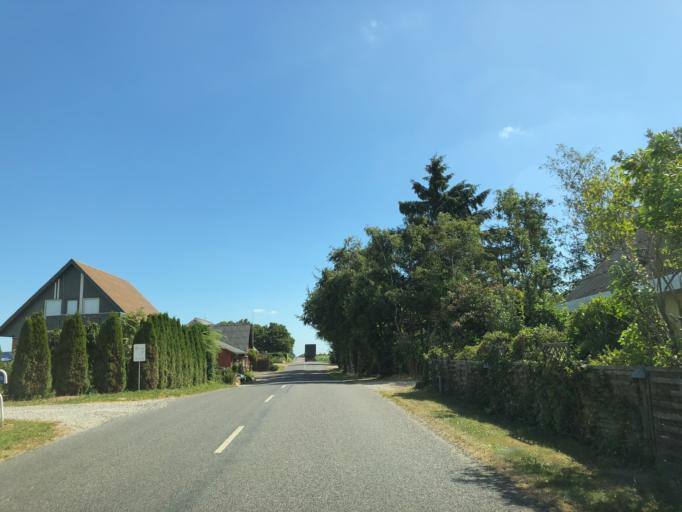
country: DK
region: North Denmark
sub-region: Vesthimmerland Kommune
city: Alestrup
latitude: 56.5776
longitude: 9.5658
